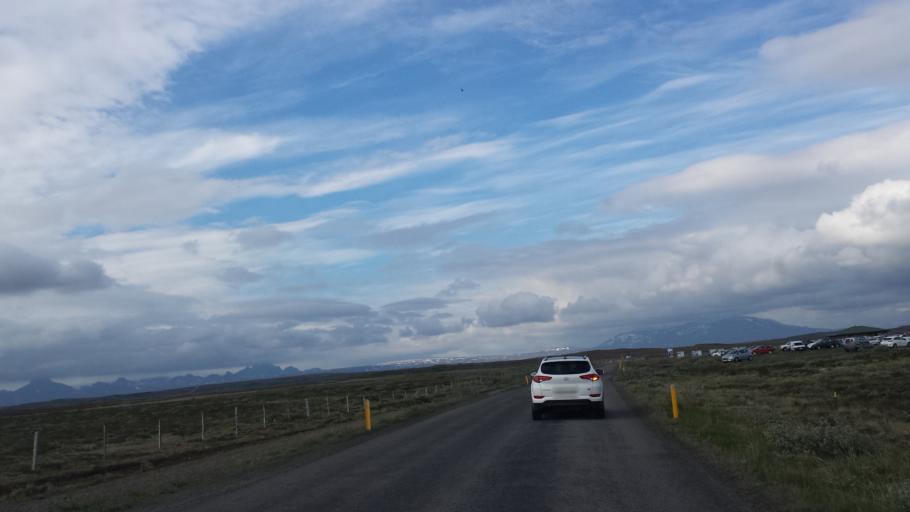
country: IS
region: South
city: Vestmannaeyjar
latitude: 64.3242
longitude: -20.1334
